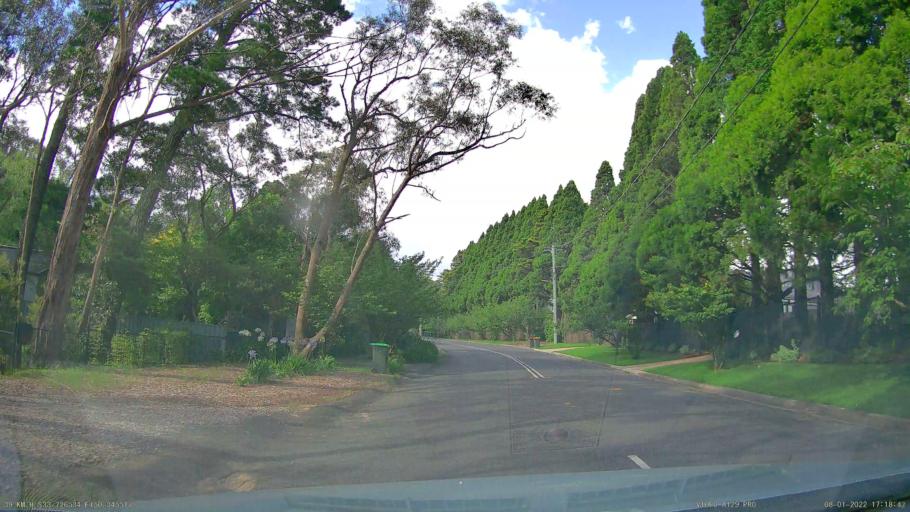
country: AU
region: New South Wales
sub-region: Blue Mountains Municipality
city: Leura
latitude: -33.7264
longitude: 150.3456
